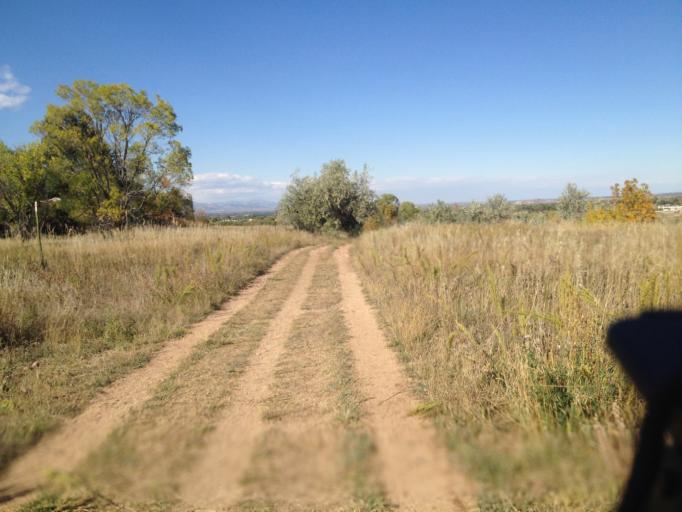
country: US
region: Colorado
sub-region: Boulder County
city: Boulder
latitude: 39.9753
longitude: -105.2365
